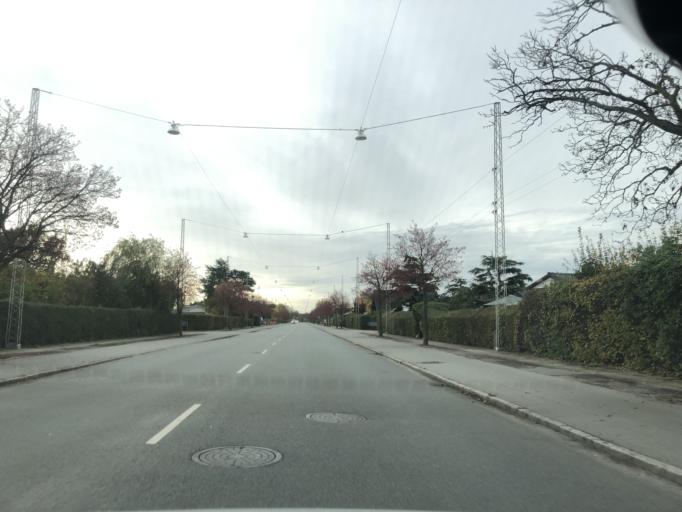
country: DK
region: Capital Region
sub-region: Tarnby Kommune
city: Tarnby
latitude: 55.5954
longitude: 12.5820
